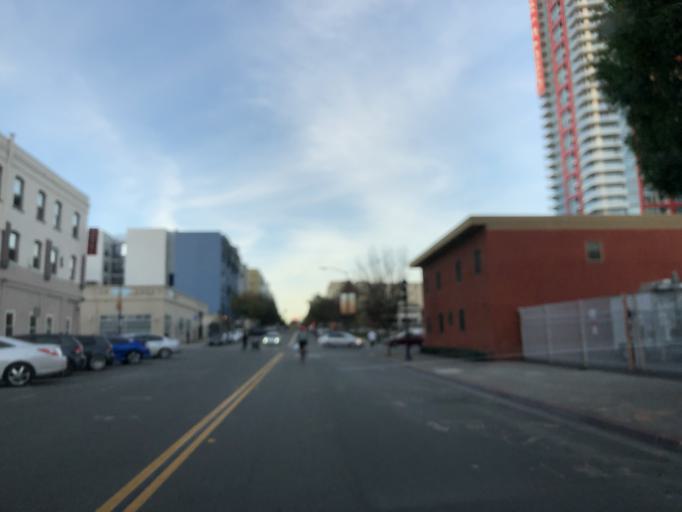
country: US
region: California
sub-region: San Diego County
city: San Diego
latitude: 32.7090
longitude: -117.1519
